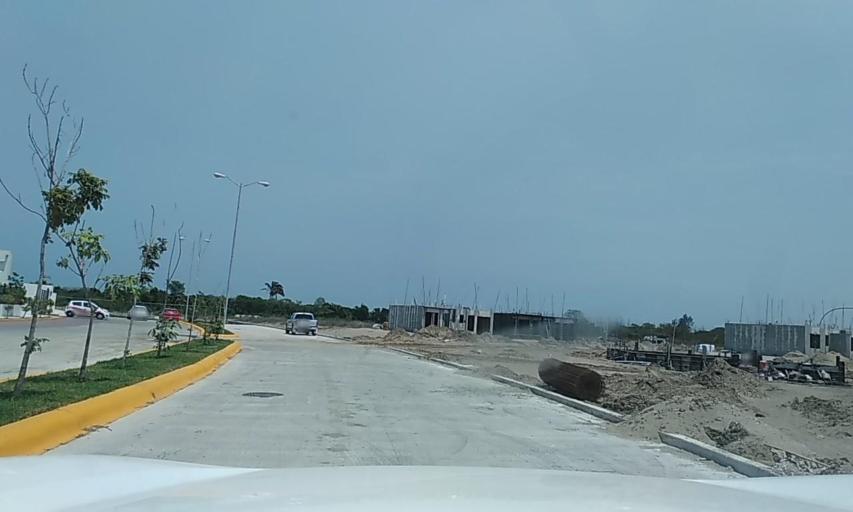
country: MX
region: Veracruz
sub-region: Veracruz
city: Hacienda Sotavento
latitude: 19.1235
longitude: -96.1691
